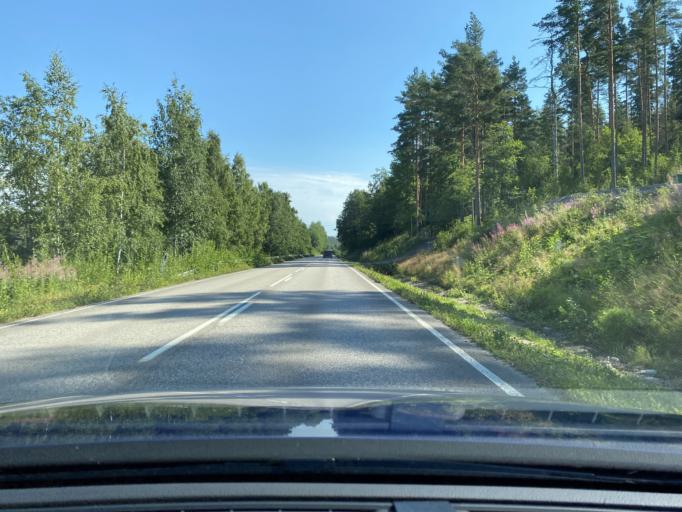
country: FI
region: Central Finland
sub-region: Jaemsae
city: Jaemsae
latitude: 61.8931
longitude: 25.3374
